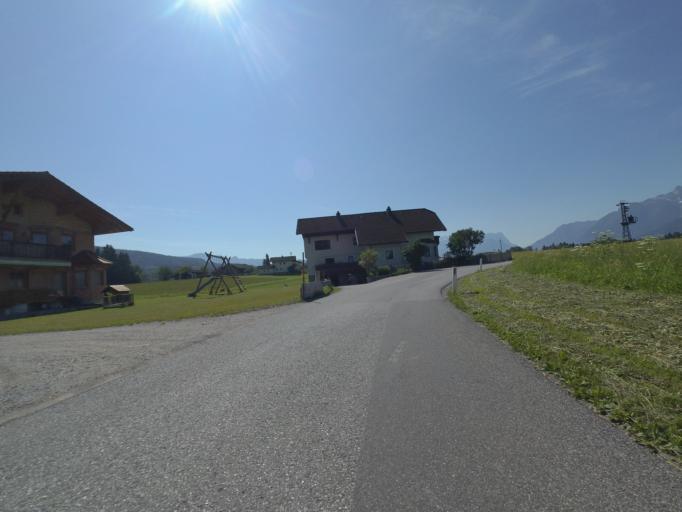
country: AT
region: Salzburg
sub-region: Politischer Bezirk Hallein
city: Adnet
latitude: 47.6796
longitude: 13.1374
